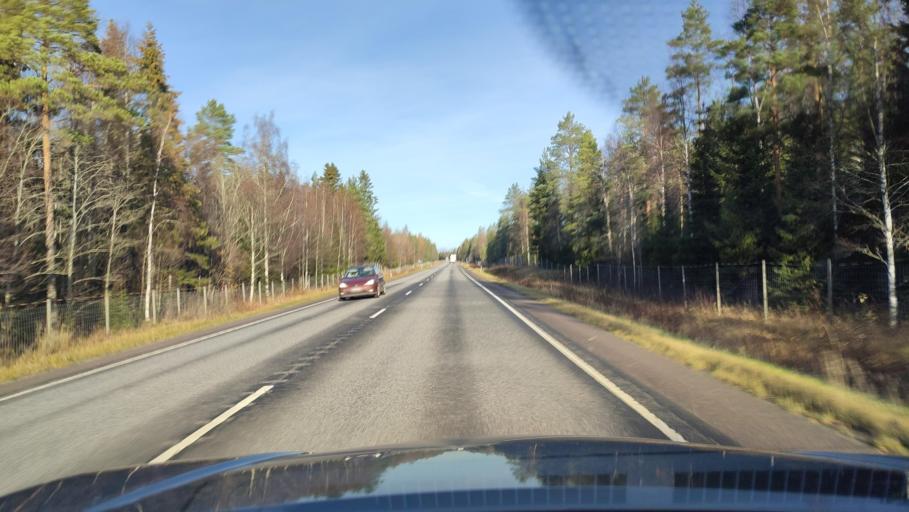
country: FI
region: Ostrobothnia
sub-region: Vaasa
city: Malax
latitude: 62.8278
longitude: 21.6915
